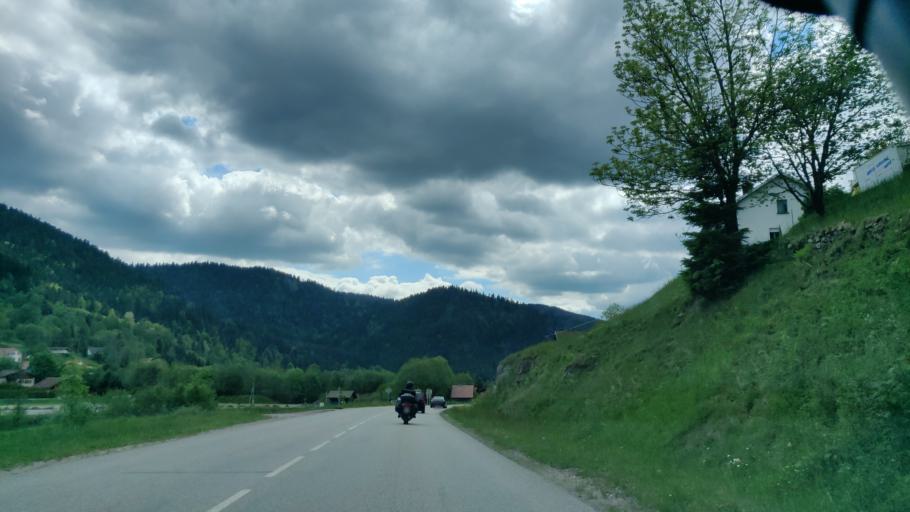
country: FR
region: Lorraine
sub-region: Departement des Vosges
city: La Bresse
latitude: 48.0046
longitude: 6.9310
